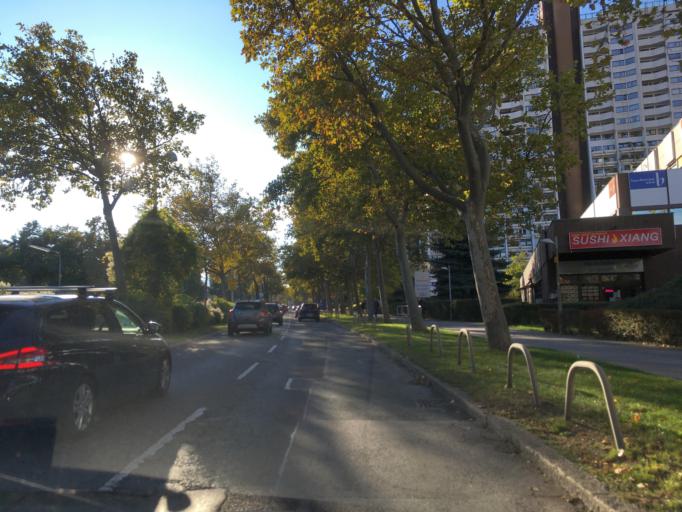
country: AT
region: Lower Austria
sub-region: Politischer Bezirk Modling
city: Vosendorf
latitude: 48.1509
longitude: 16.3156
